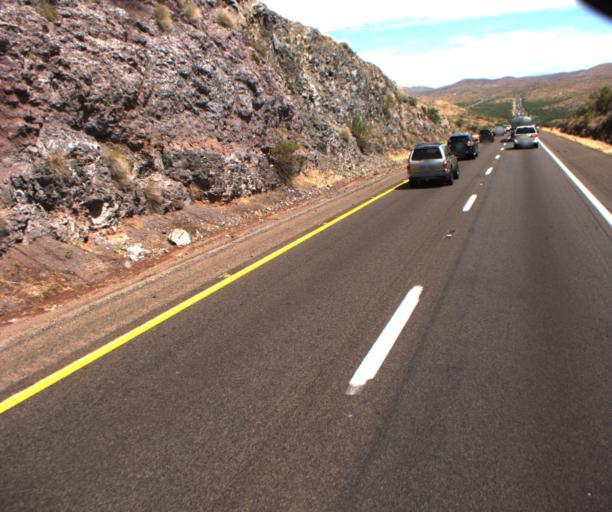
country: US
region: Arizona
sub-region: Yavapai County
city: Cordes Lakes
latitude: 34.2278
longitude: -112.1110
